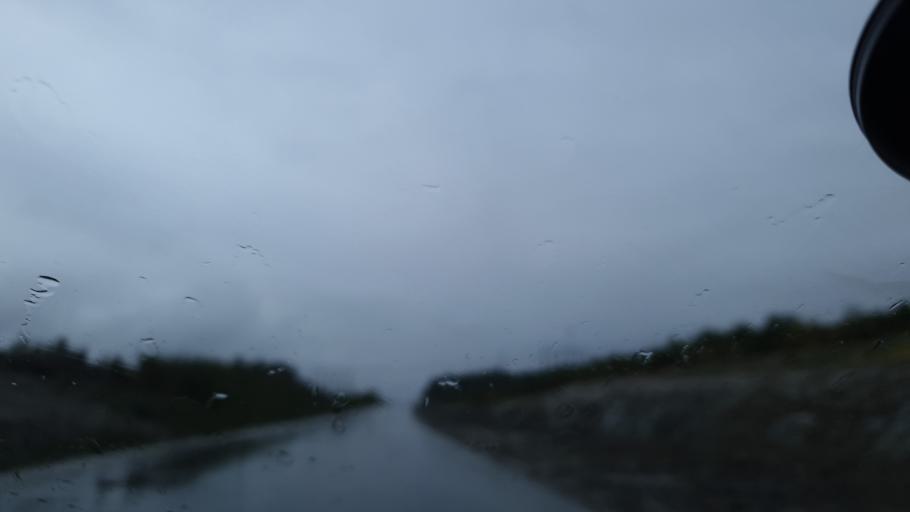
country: SE
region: Vaesterbotten
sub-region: Skelleftea Kommun
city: Soedra Bergsbyn
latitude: 64.7438
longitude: 21.0616
